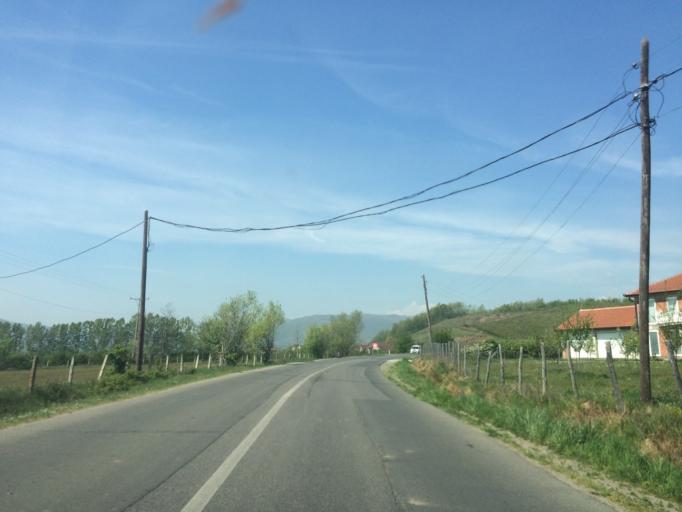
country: XK
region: Gjakova
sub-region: Komuna e Gjakoves
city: Gjakove
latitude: 42.3766
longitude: 20.3815
